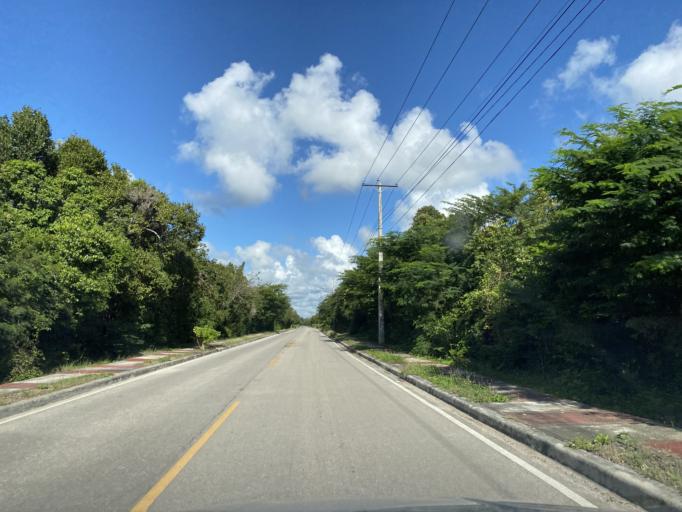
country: DO
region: La Altagracia
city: San Rafael del Yuma
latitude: 18.3358
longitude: -68.8095
